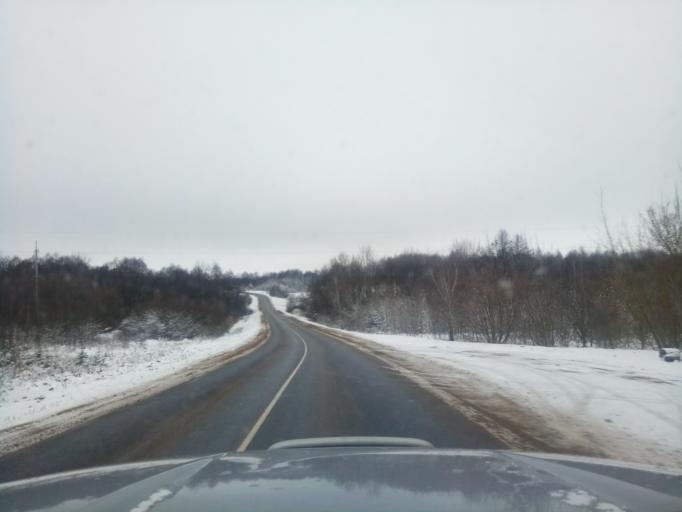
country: BY
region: Minsk
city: Kapyl'
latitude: 53.1511
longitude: 27.1219
